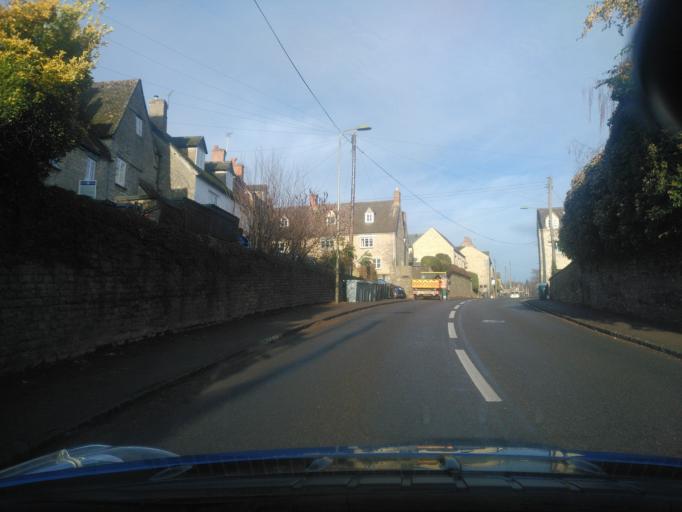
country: GB
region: England
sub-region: Oxfordshire
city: Woodstock
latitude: 51.8507
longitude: -1.3604
